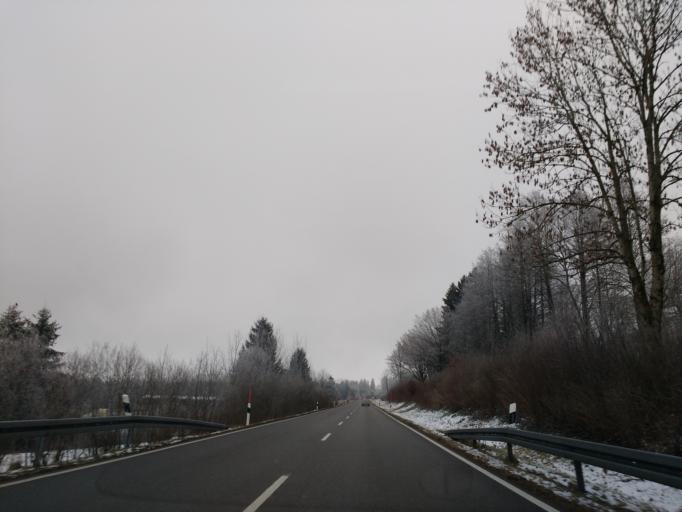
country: DE
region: Bavaria
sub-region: Swabia
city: Oy-Mittelberg
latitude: 47.6467
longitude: 10.4650
